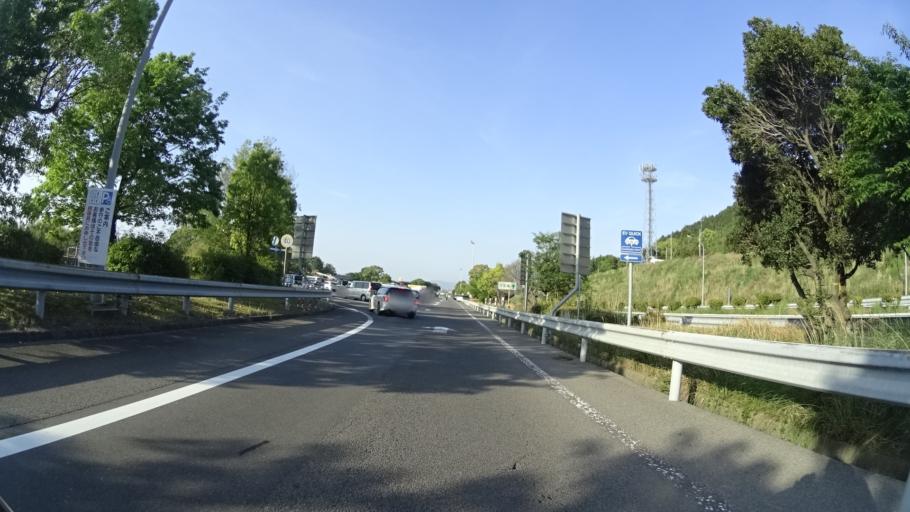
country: JP
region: Ehime
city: Kawanoecho
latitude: 34.0559
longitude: 133.6362
